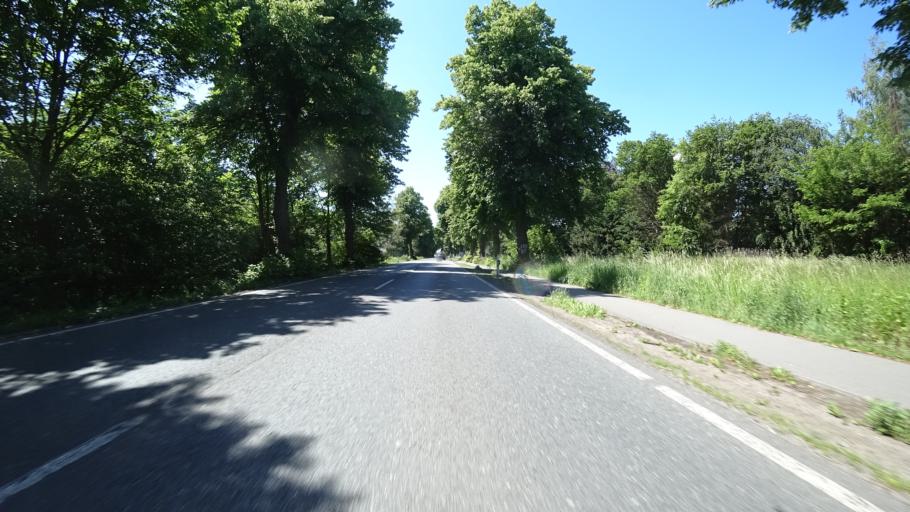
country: DE
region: North Rhine-Westphalia
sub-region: Regierungsbezirk Detmold
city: Guetersloh
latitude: 51.9252
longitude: 8.4041
